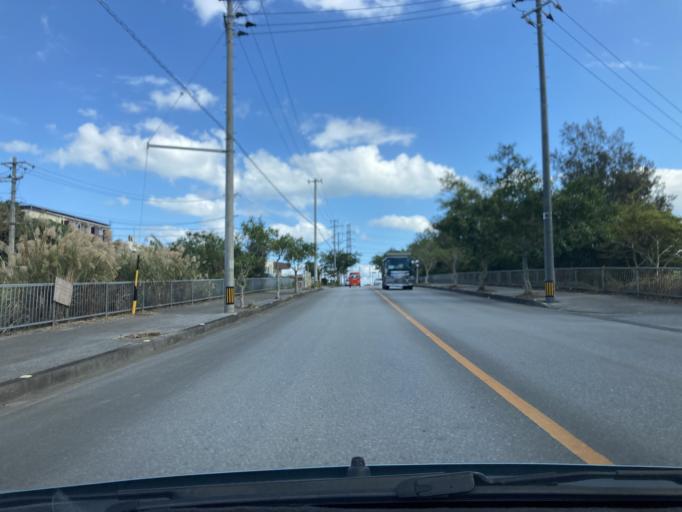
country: JP
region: Okinawa
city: Gushikawa
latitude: 26.3683
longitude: 127.8378
